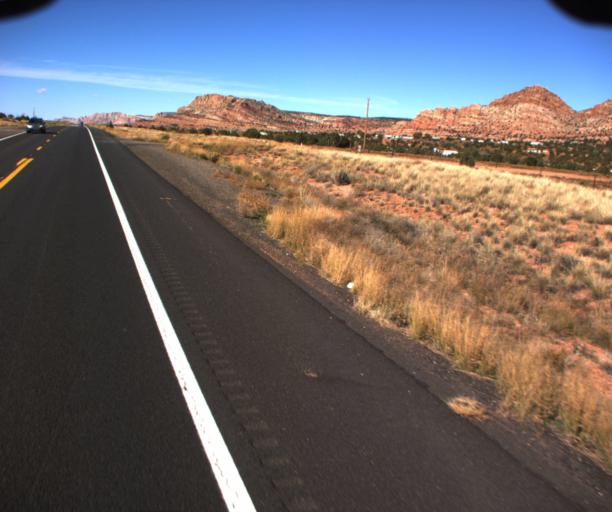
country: US
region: Arizona
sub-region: Coconino County
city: Tuba City
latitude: 36.3860
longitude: -111.5217
